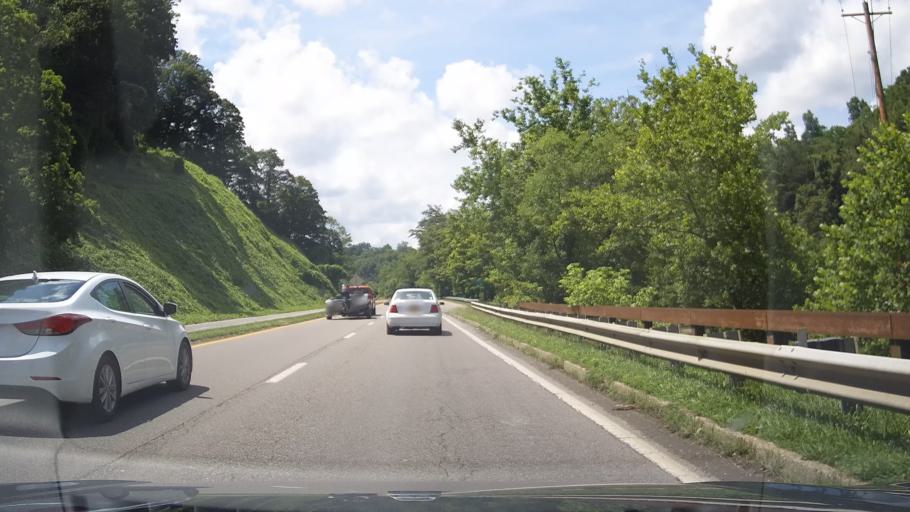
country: US
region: Virginia
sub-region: Scott County
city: Weber City
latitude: 36.6352
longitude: -82.5512
